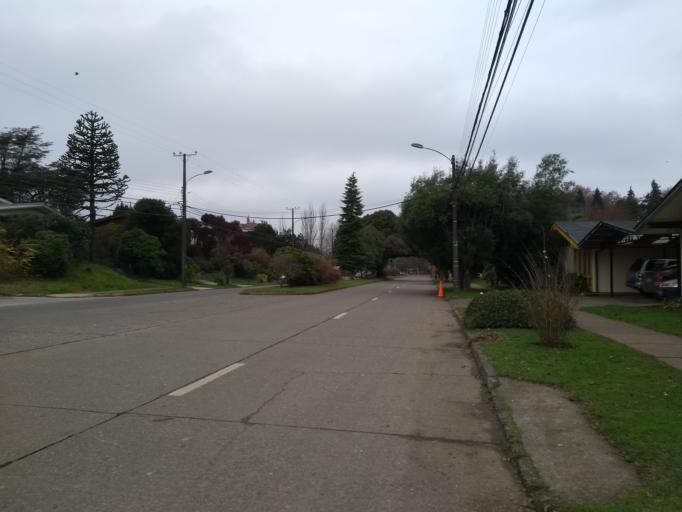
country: CL
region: Los Rios
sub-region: Provincia de Valdivia
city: Valdivia
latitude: -39.8094
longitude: -73.2601
